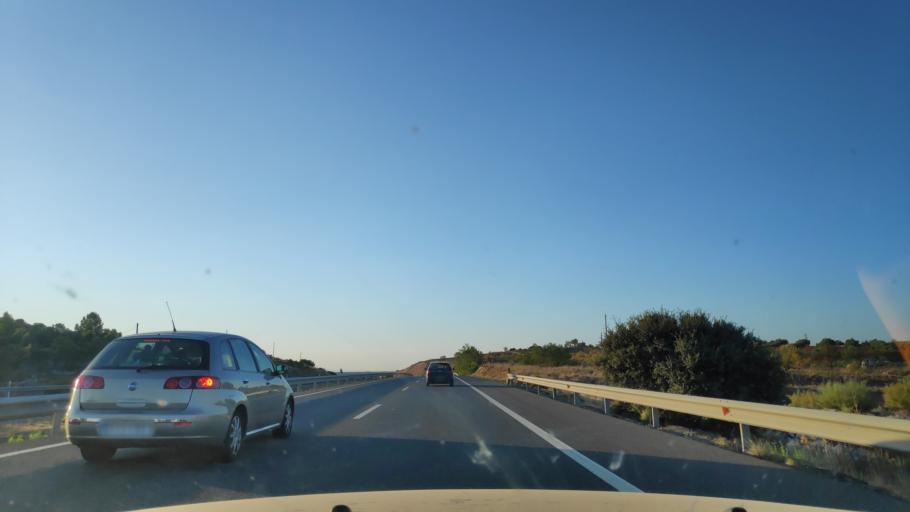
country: ES
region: Madrid
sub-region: Provincia de Madrid
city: Villarejo de Salvanes
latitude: 40.1869
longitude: -3.2981
